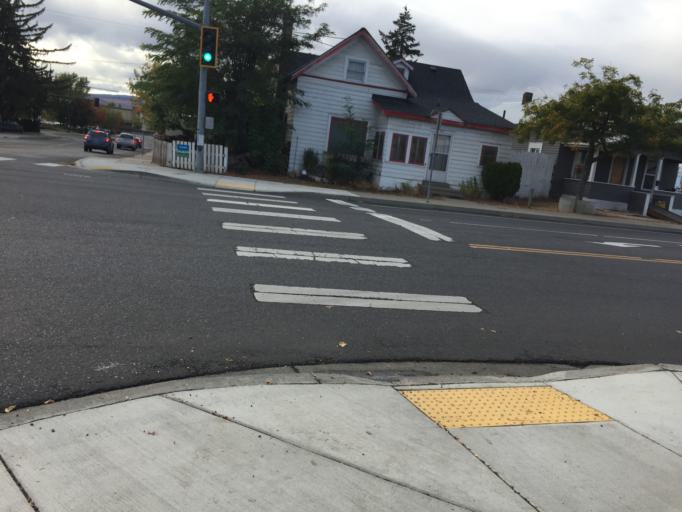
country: US
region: Washington
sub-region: Kittitas County
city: Ellensburg
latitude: 46.9914
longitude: -120.5483
